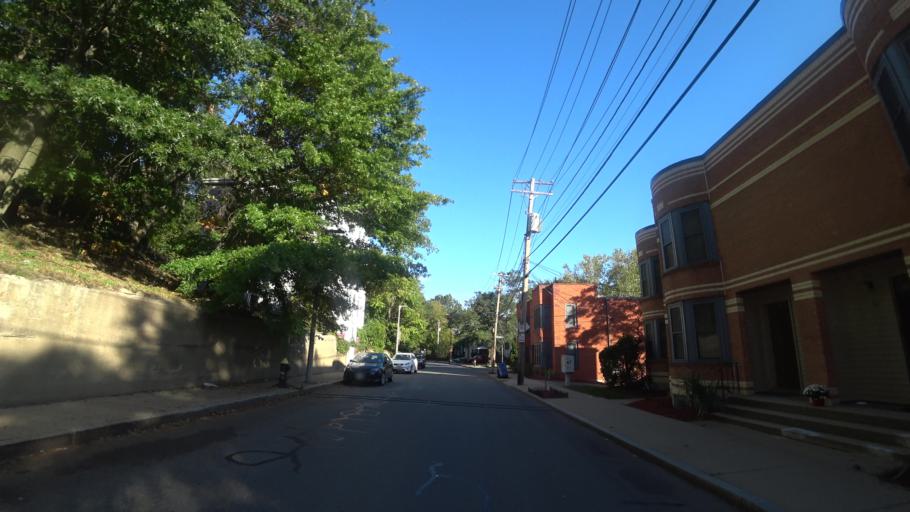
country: US
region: Massachusetts
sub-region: Norfolk County
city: Brookline
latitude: 42.3283
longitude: -71.1071
